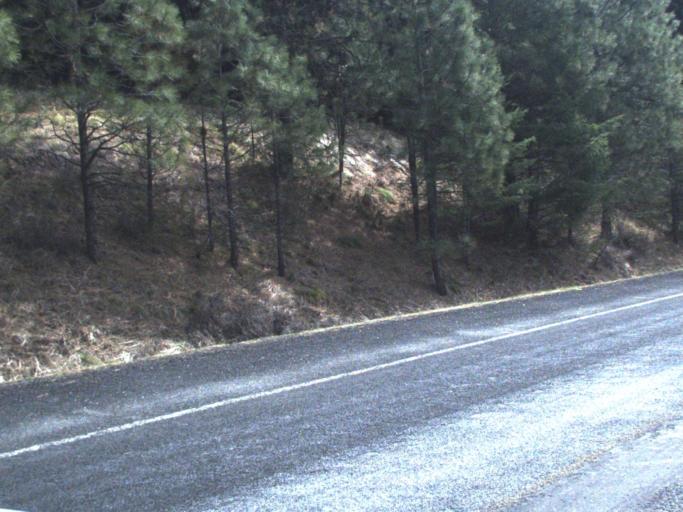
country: US
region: Washington
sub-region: Kittitas County
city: Cle Elum
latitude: 46.9258
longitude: -121.0459
